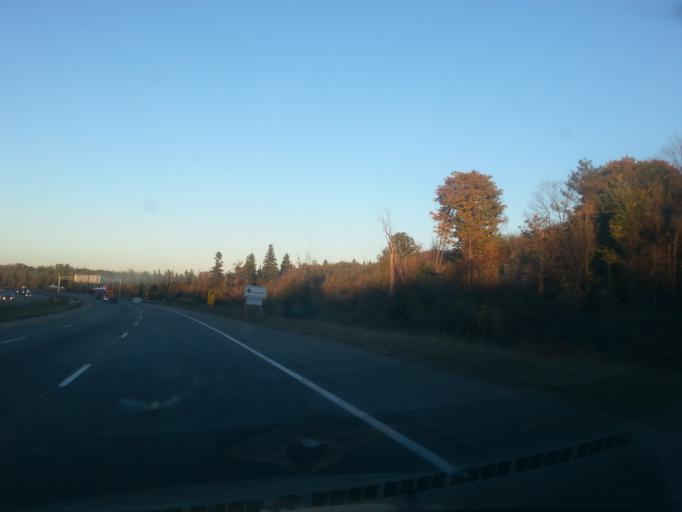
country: CA
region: Ontario
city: Barrie
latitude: 44.4182
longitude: -79.6582
